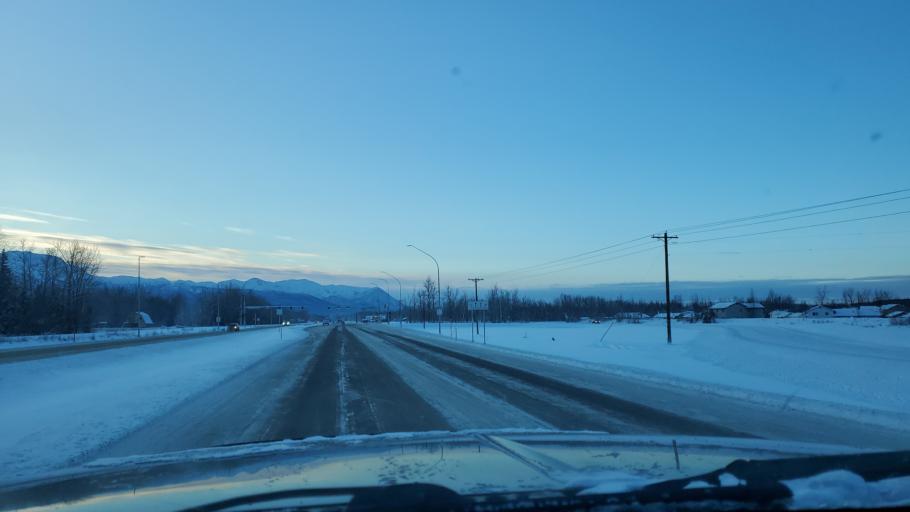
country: US
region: Alaska
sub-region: Matanuska-Susitna Borough
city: Palmer
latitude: 61.5729
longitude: -149.1473
